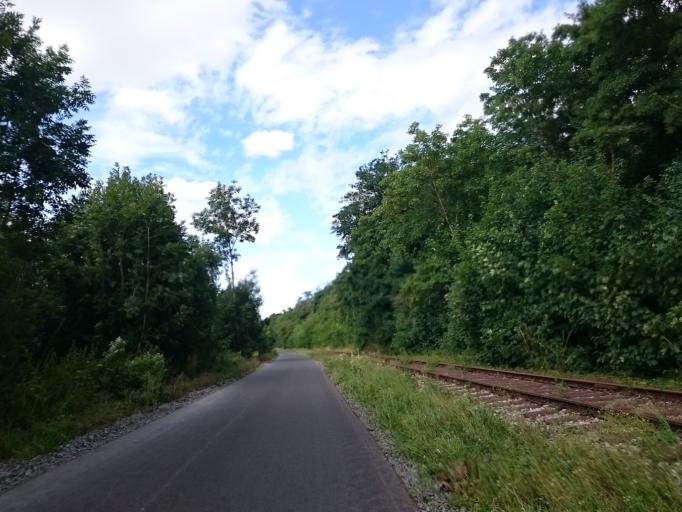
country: FR
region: Lower Normandy
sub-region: Departement du Calvados
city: Clinchamps-sur-Orne
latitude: 49.0725
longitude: -0.4311
